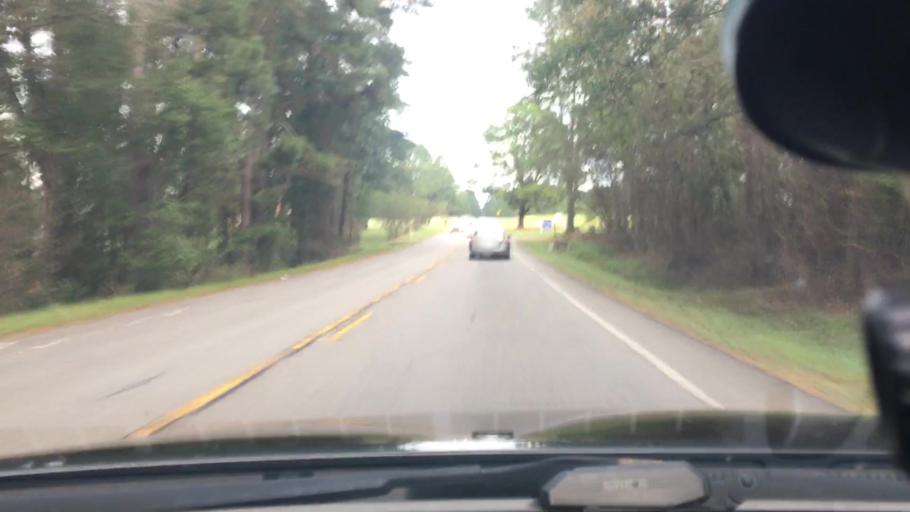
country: US
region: North Carolina
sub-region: Moore County
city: Carthage
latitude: 35.3704
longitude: -79.3059
